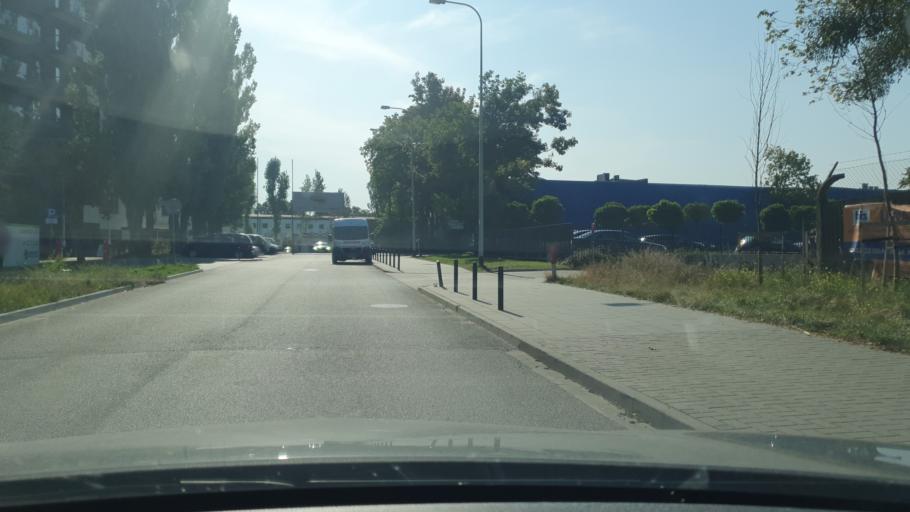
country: PL
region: Pomeranian Voivodeship
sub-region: Sopot
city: Sopot
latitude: 54.4018
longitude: 18.5874
